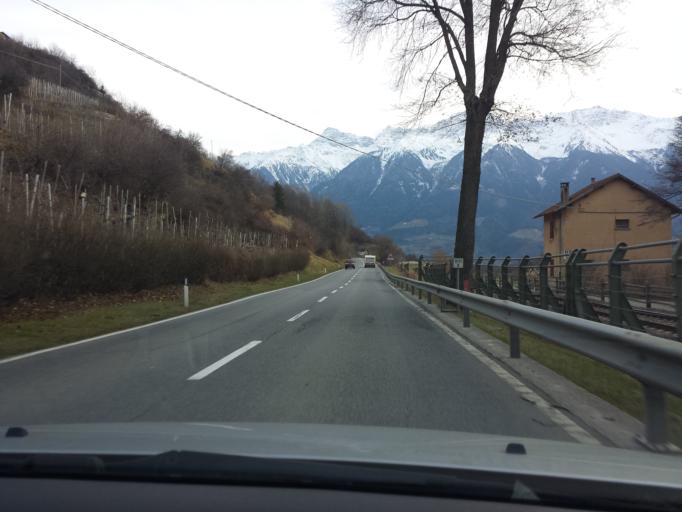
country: IT
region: Trentino-Alto Adige
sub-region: Bolzano
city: Sluderno
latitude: 46.6516
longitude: 10.5903
